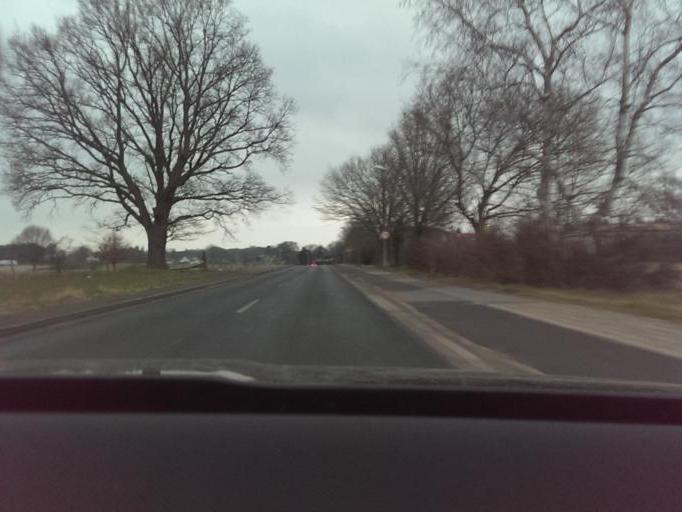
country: DE
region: Lower Saxony
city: Elze
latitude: 52.5560
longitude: 9.7297
